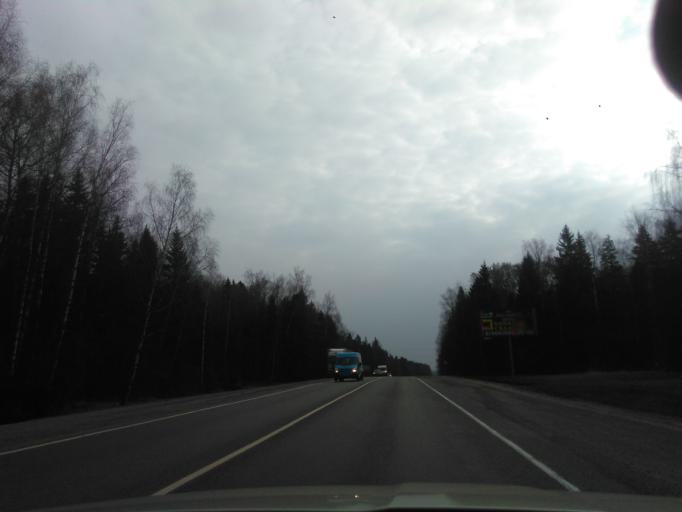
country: RU
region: Moskovskaya
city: Yermolino
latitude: 56.1377
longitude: 37.4629
